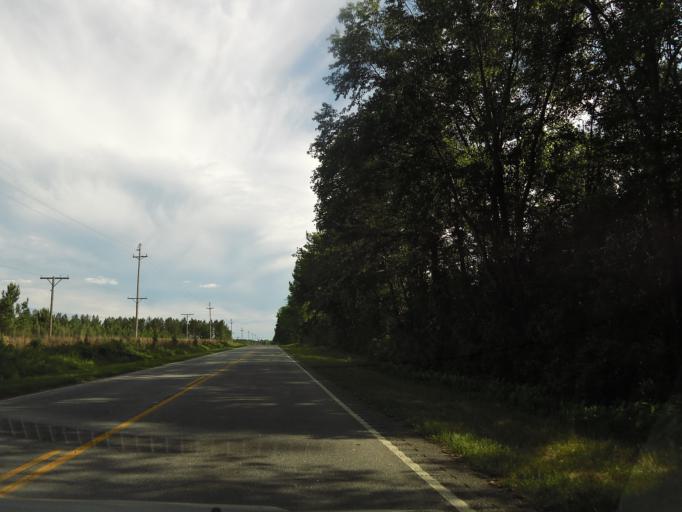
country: US
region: South Carolina
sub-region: Allendale County
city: Fairfax
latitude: 32.8865
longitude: -81.2382
